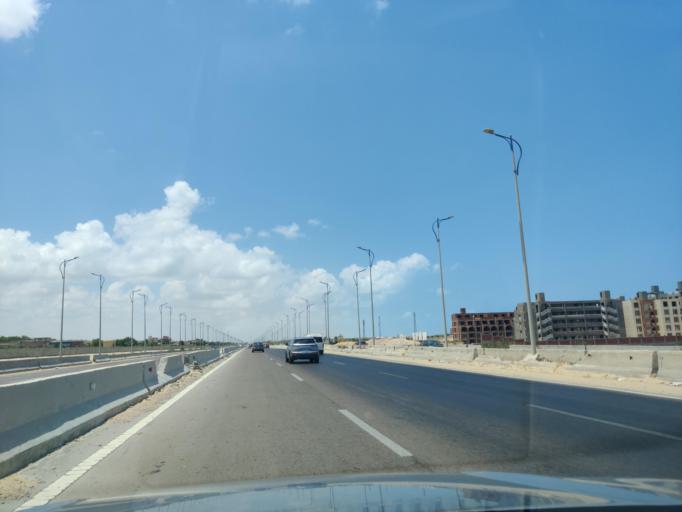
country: EG
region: Muhafazat Matruh
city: Al `Alamayn
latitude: 30.9206
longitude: 29.4558
